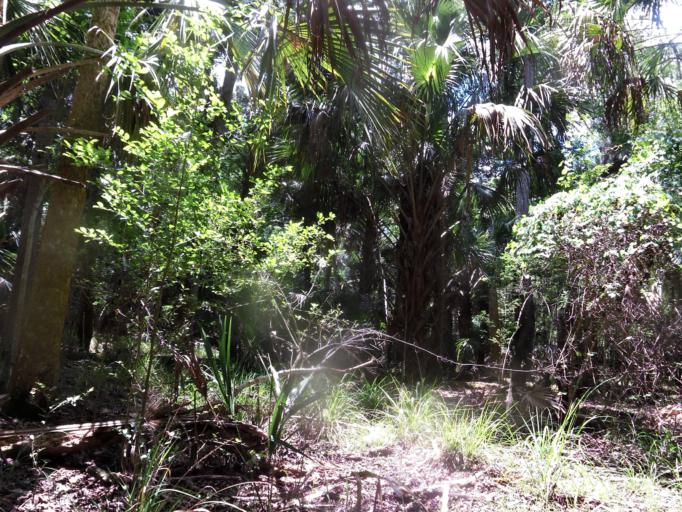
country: US
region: Florida
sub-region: Flagler County
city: Flagler Beach
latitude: 29.4264
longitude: -81.1426
